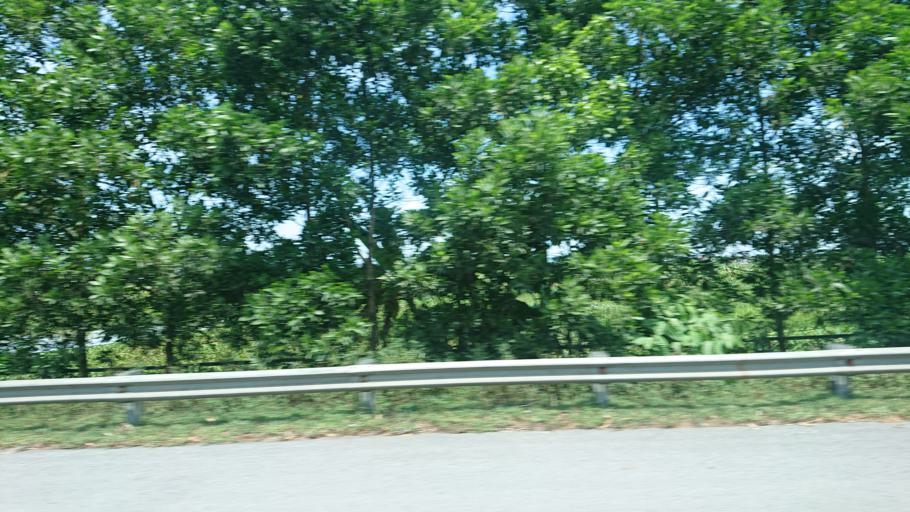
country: VN
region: Ha Nam
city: Thanh Pho Phu Ly
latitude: 20.5589
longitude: 105.9490
